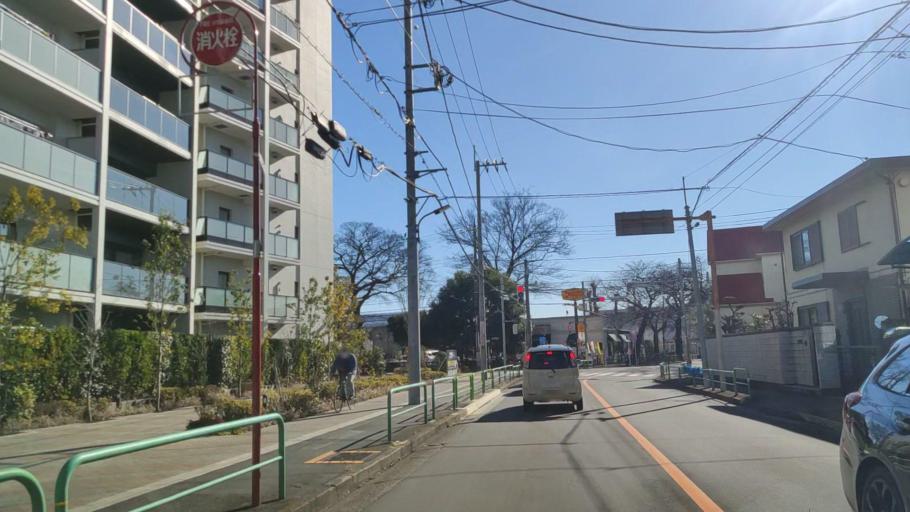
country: JP
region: Tokyo
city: Musashino
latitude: 35.7214
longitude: 139.5687
